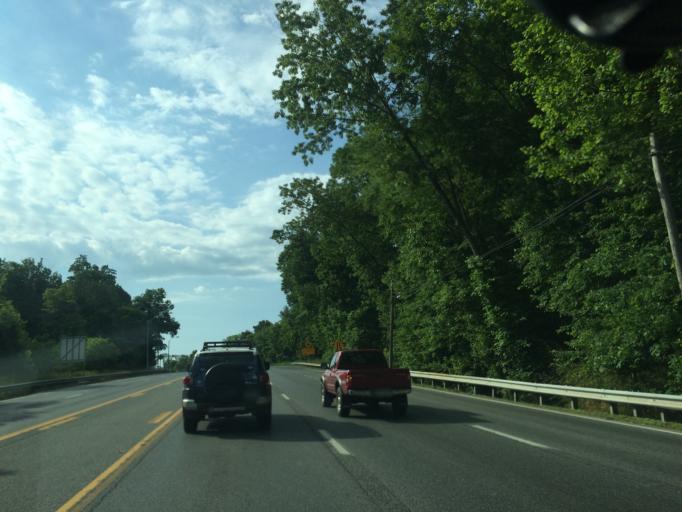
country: US
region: Maryland
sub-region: Baltimore County
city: Reisterstown
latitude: 39.4833
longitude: -76.8585
